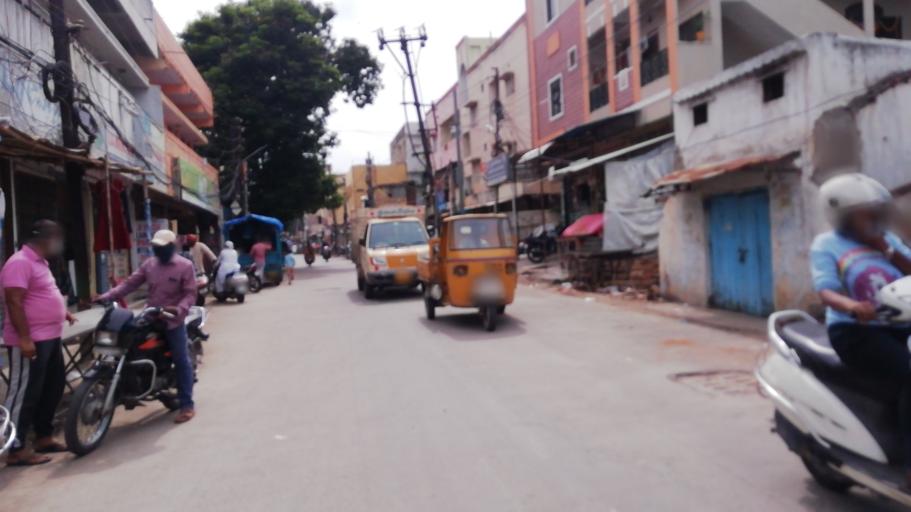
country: IN
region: Telangana
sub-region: Hyderabad
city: Malkajgiri
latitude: 17.4146
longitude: 78.5032
